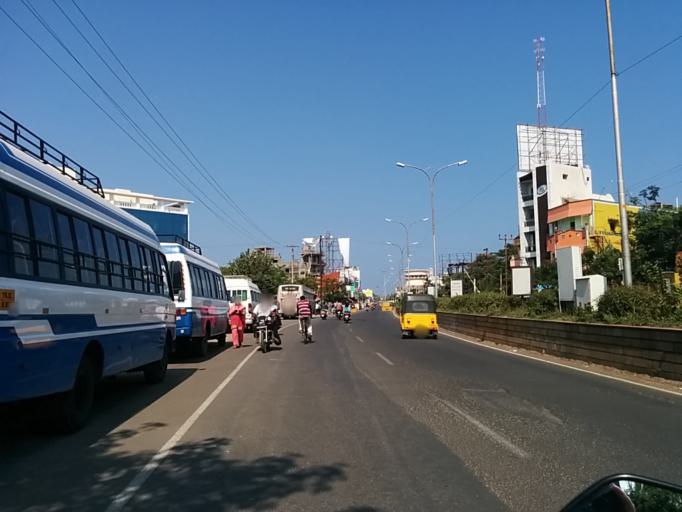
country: IN
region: Pondicherry
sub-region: Puducherry
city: Puducherry
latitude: 11.9509
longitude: 79.8157
